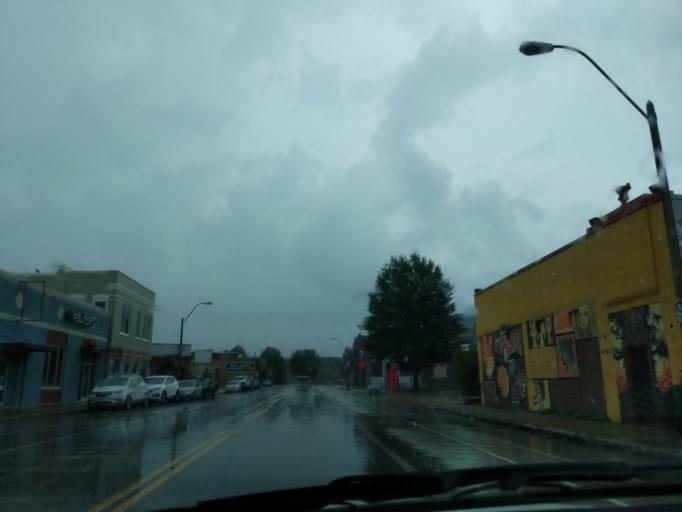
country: US
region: Tennessee
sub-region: Shelby County
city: Memphis
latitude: 35.1403
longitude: -90.0393
